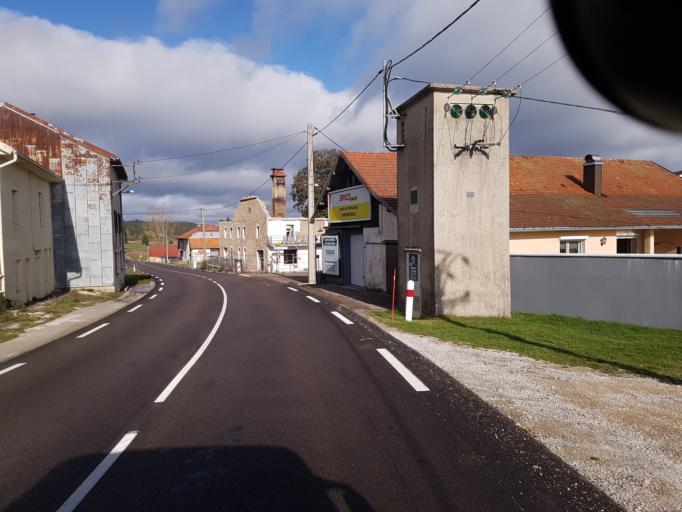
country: FR
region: Franche-Comte
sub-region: Departement du Jura
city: Morbier
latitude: 46.6074
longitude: 5.9624
